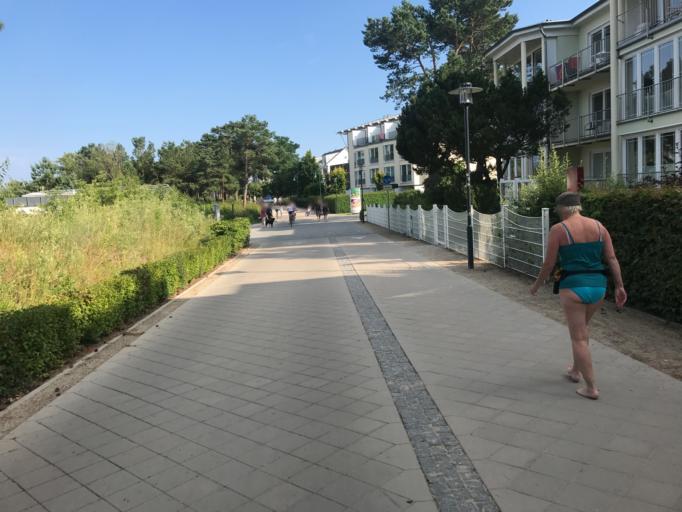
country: DE
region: Mecklenburg-Vorpommern
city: Seebad Bansin
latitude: 53.9681
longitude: 14.1509
